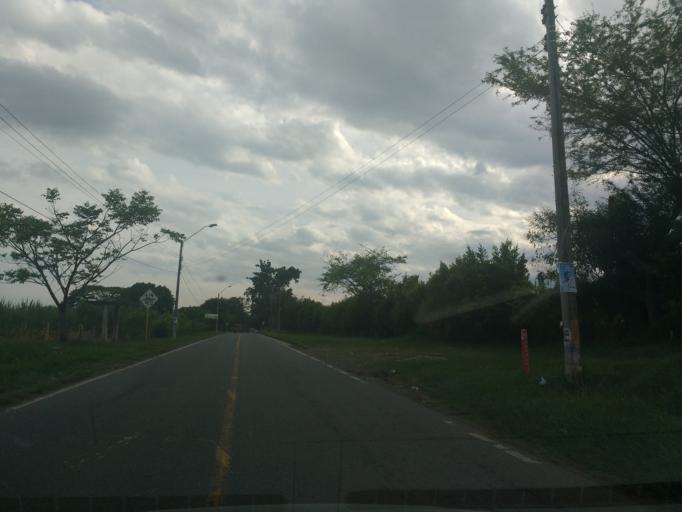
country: CO
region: Cauca
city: Miranda
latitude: 3.2396
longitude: -76.2307
